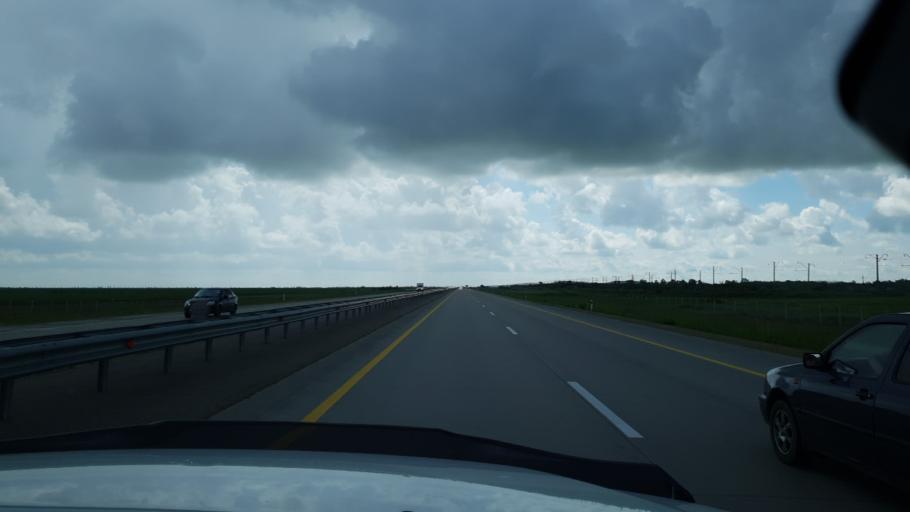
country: KZ
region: Qaraghandy
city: Osakarovka
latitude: 50.6023
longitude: 72.4958
